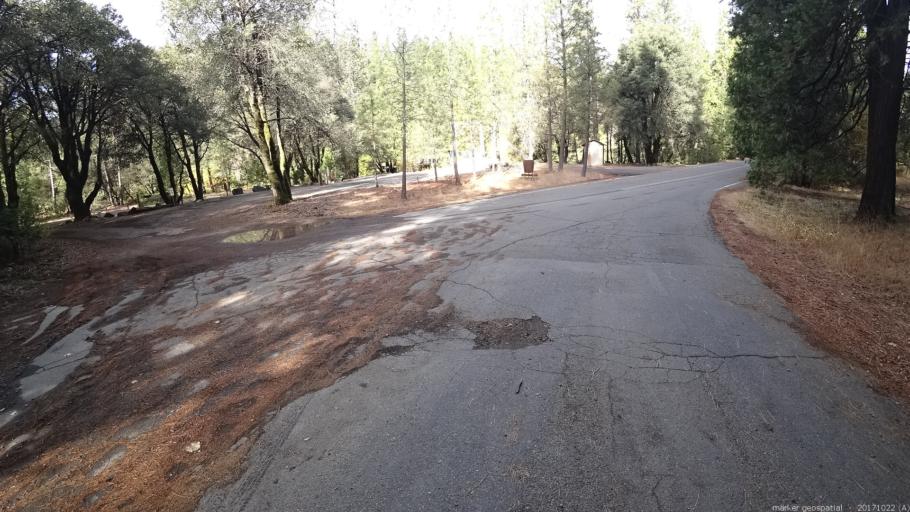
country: US
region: California
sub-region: Siskiyou County
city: Dunsmuir
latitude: 41.0629
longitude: -122.3593
